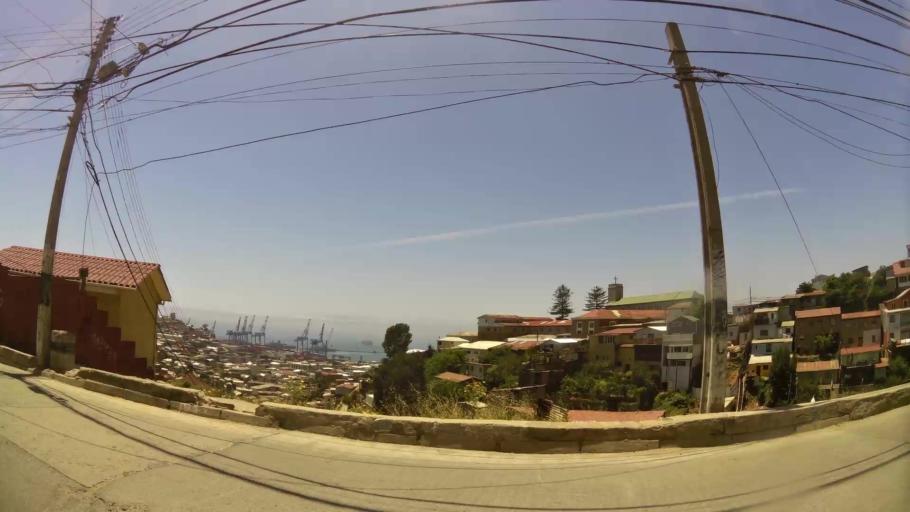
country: CL
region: Valparaiso
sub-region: Provincia de Valparaiso
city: Valparaiso
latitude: -33.0419
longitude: -71.6366
